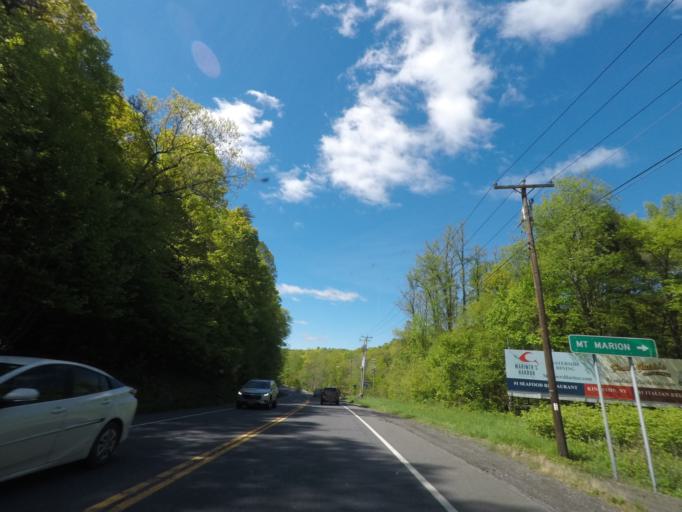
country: US
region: New York
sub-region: Ulster County
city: Glasco
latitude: 42.0390
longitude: -73.9699
